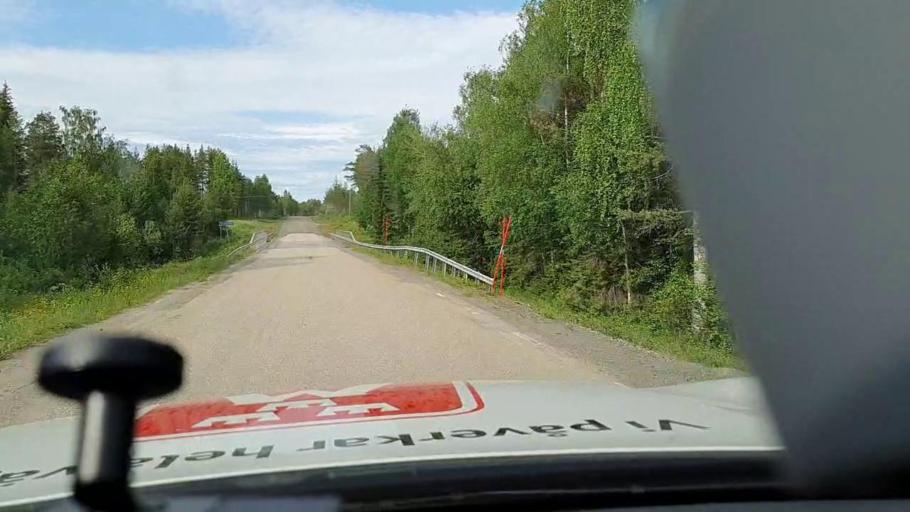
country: SE
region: Norrbotten
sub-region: Alvsbyns Kommun
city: AElvsbyn
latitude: 66.1497
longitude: 21.0305
